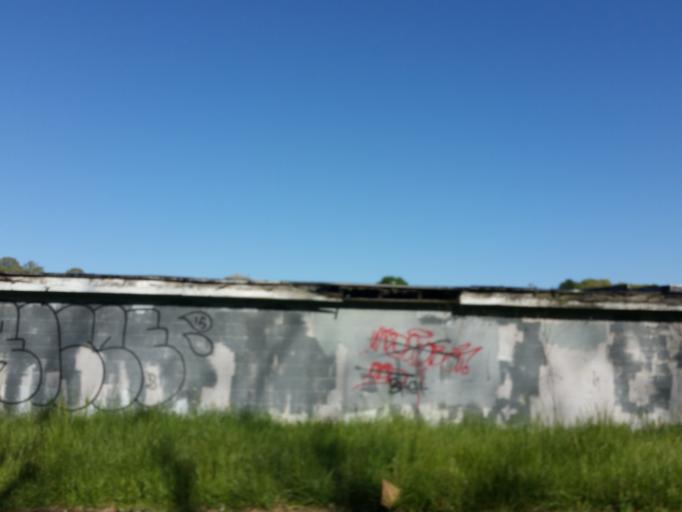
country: US
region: North Carolina
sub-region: Buncombe County
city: Asheville
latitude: 35.5795
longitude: -82.5676
